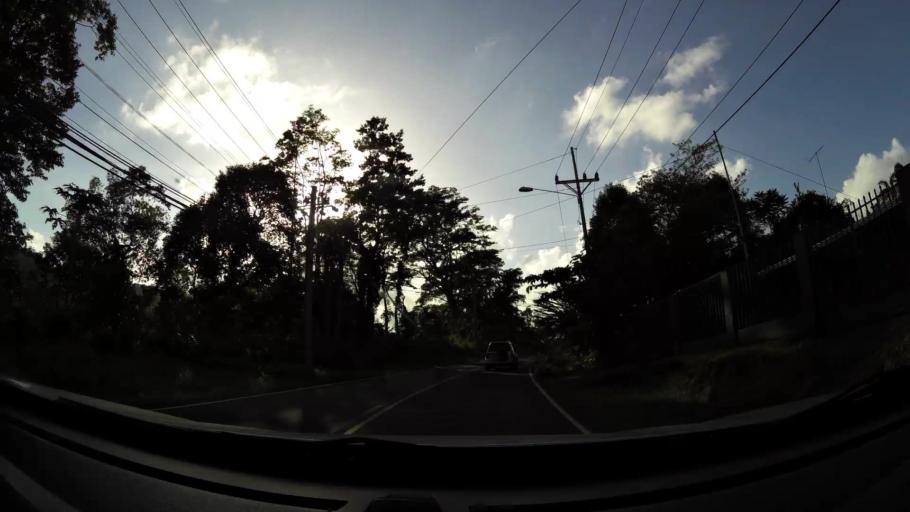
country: CR
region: Limon
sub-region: Canton de Siquirres
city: Siquirres
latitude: 10.0937
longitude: -83.5130
